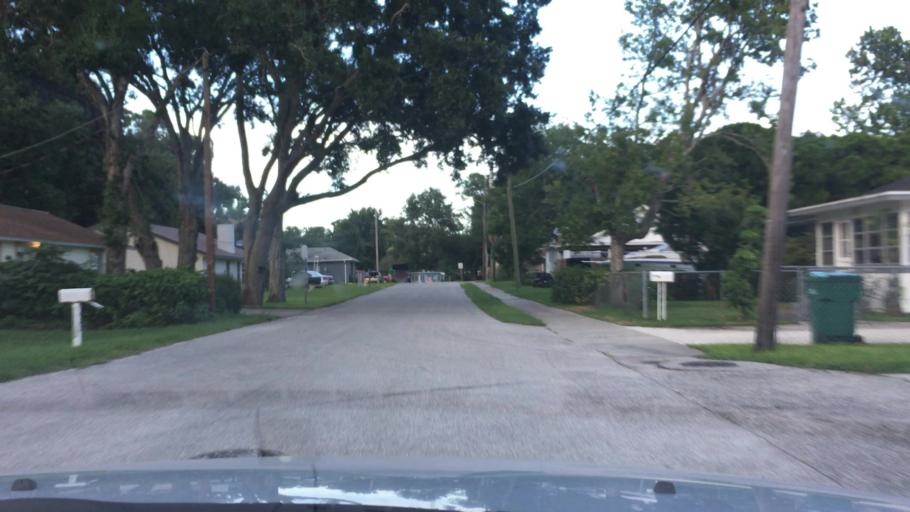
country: US
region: Florida
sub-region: Volusia County
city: Holly Hill
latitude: 29.2302
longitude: -81.0425
